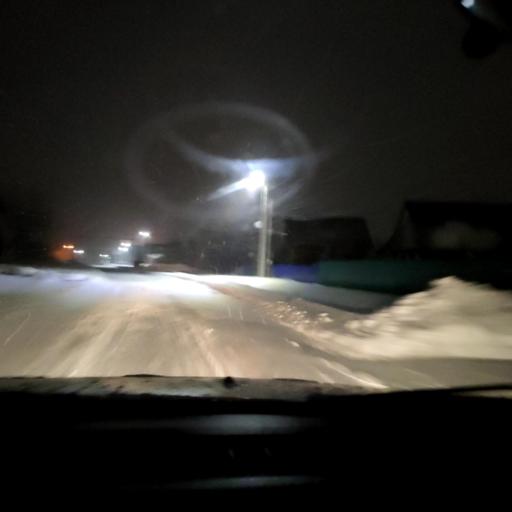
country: RU
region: Bashkortostan
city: Iglino
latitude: 54.8241
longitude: 56.3833
